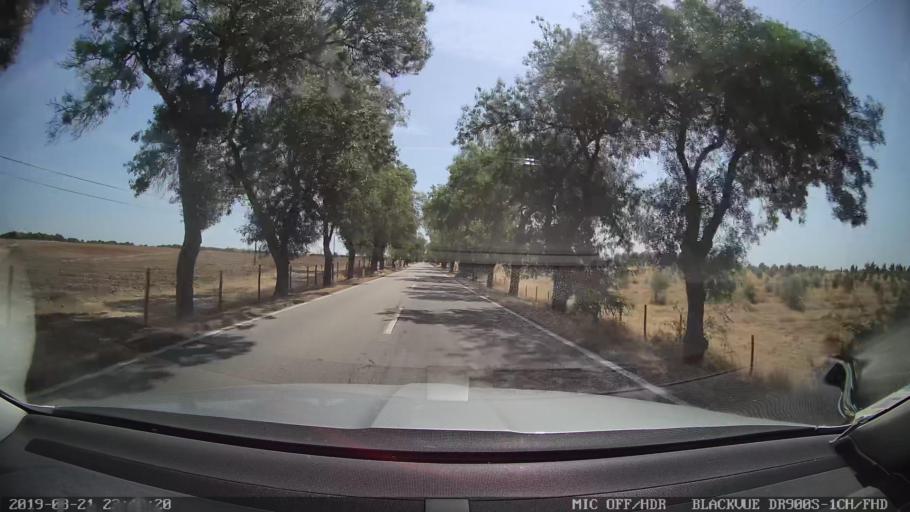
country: PT
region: Castelo Branco
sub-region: Idanha-A-Nova
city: Idanha-a-Nova
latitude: 39.8504
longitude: -7.2967
